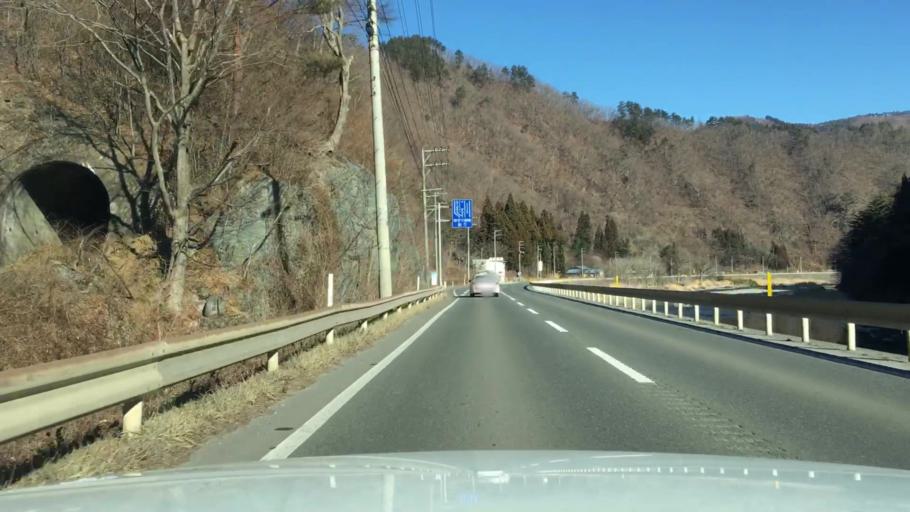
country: JP
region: Iwate
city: Miyako
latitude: 39.6125
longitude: 141.7882
